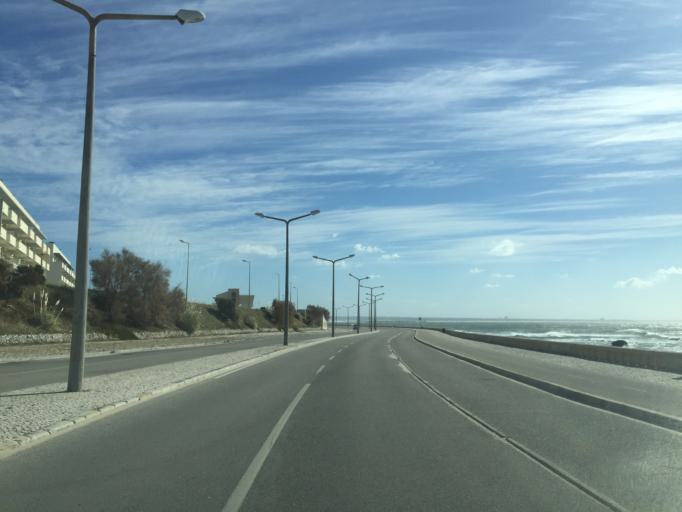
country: PT
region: Coimbra
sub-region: Figueira da Foz
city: Buarcos
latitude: 40.1746
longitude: -8.8951
